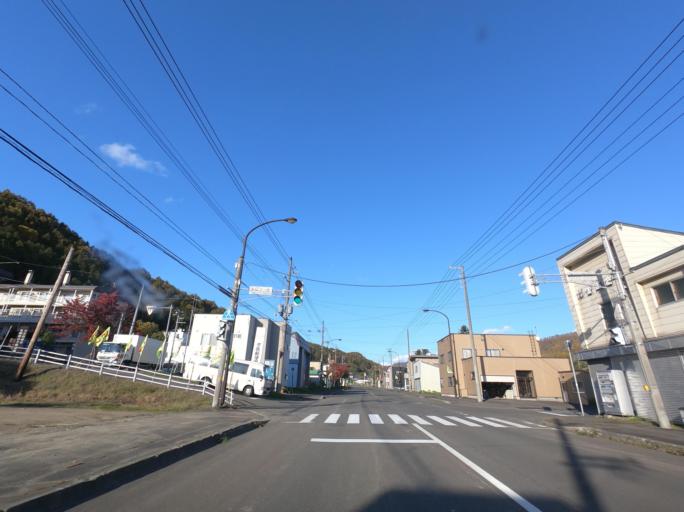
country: JP
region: Hokkaido
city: Iwamizawa
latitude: 43.0488
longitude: 141.9652
